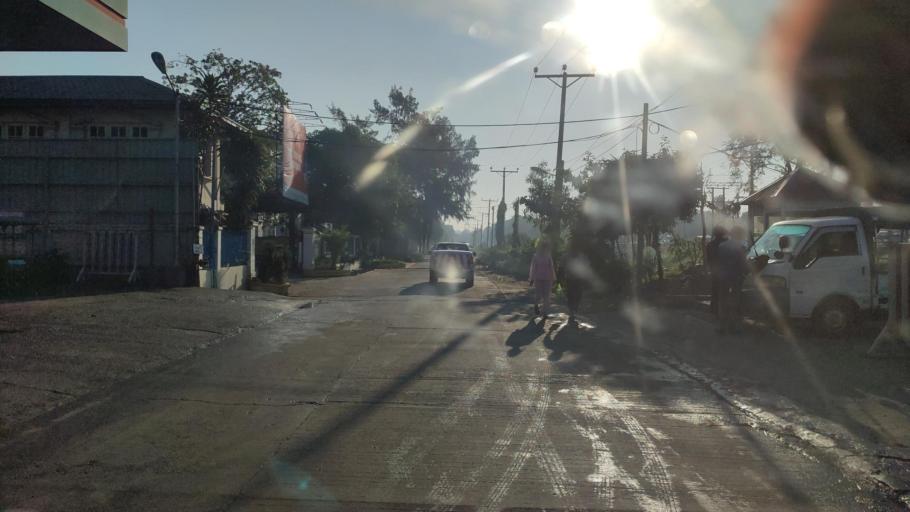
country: MM
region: Yangon
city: Yangon
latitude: 16.8586
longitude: 96.0780
